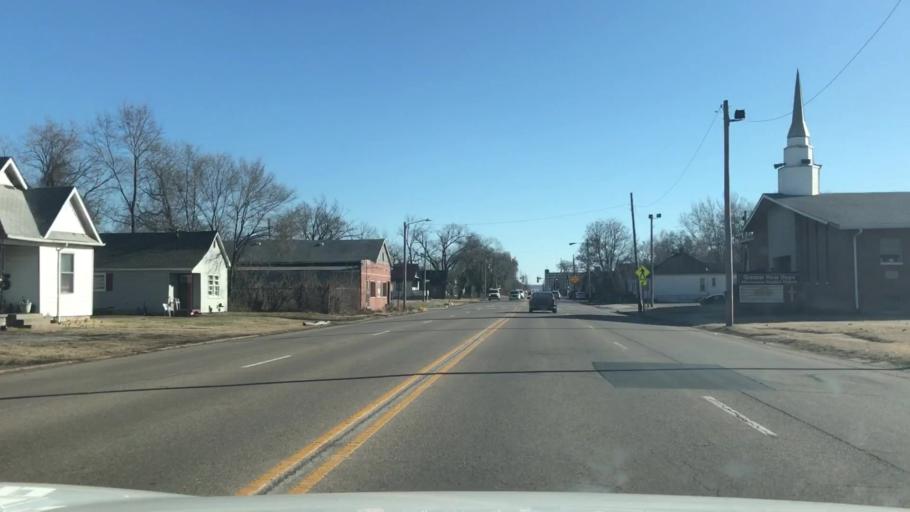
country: US
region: Illinois
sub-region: Saint Clair County
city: East Saint Louis
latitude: 38.6074
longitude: -90.1367
